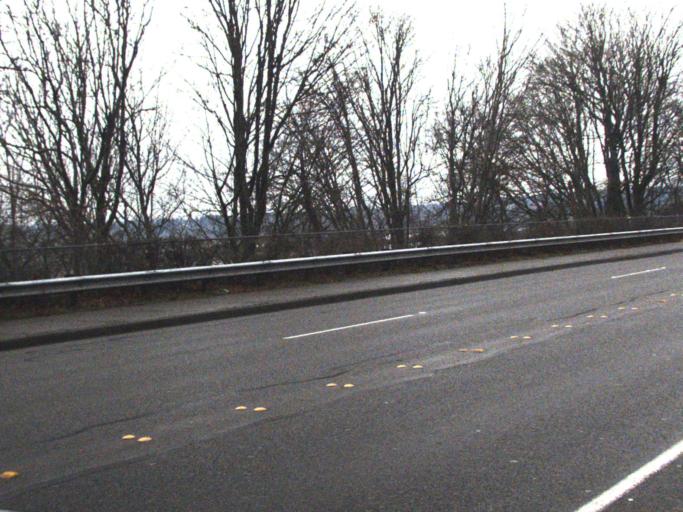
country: US
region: Washington
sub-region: Snohomish County
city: Everett
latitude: 48.0160
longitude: -122.1965
